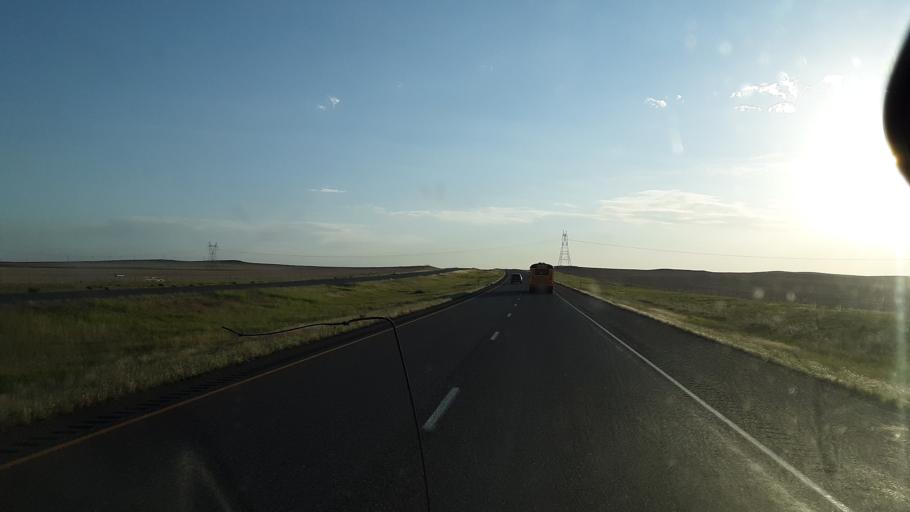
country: US
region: Montana
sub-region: Big Horn County
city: Hardin
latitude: 45.7463
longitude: -107.6852
